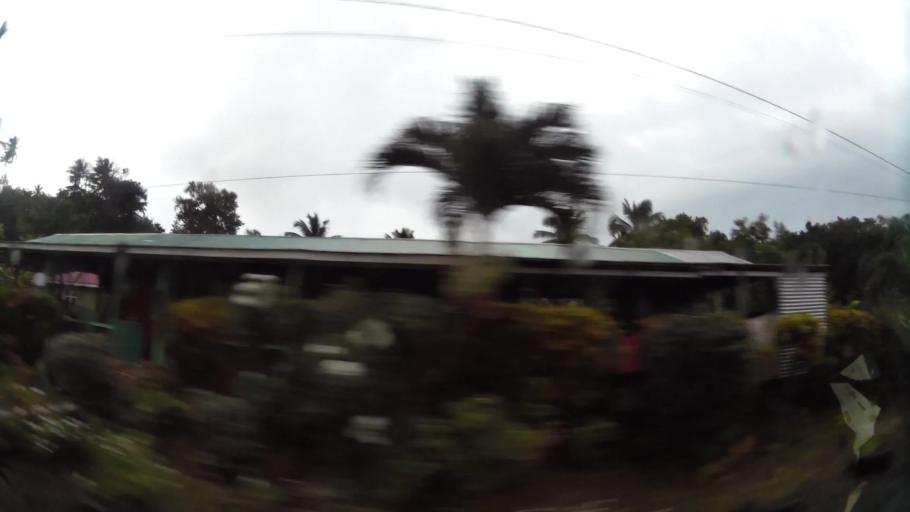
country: DM
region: Saint Andrew
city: Wesley
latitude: 15.5546
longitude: -61.3075
